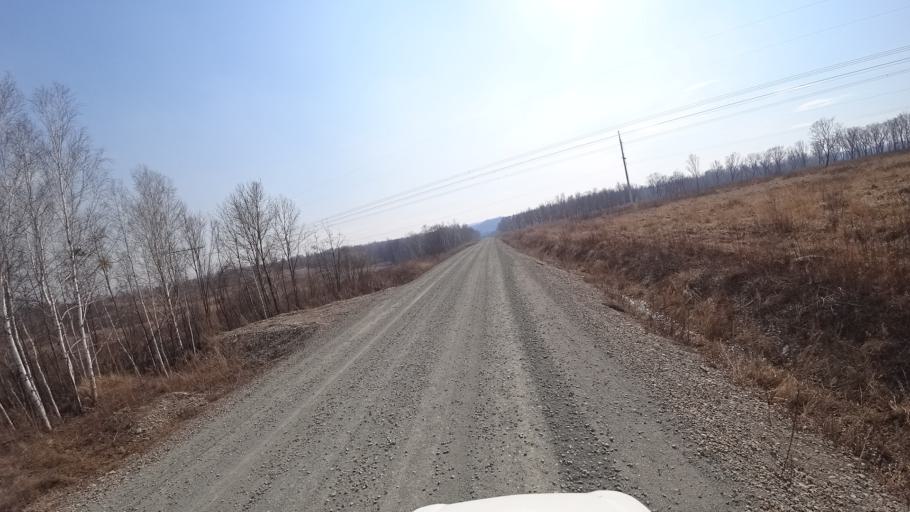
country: RU
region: Amur
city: Novobureyskiy
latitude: 49.8035
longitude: 129.9623
